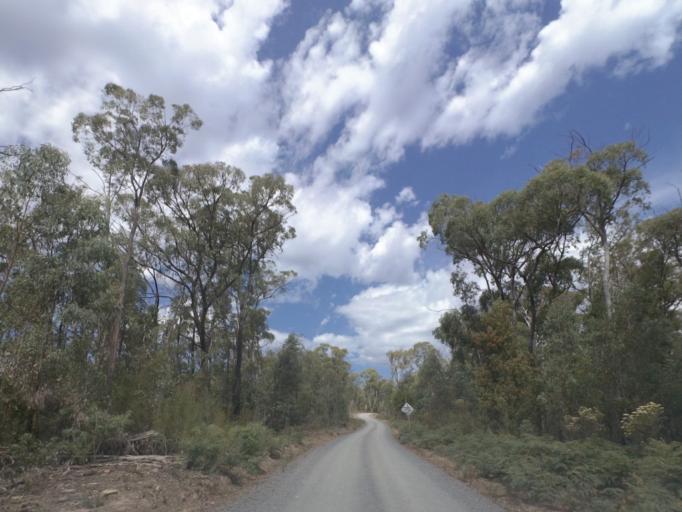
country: AU
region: Victoria
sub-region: Murrindindi
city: Alexandra
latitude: -37.3822
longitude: 145.7502
